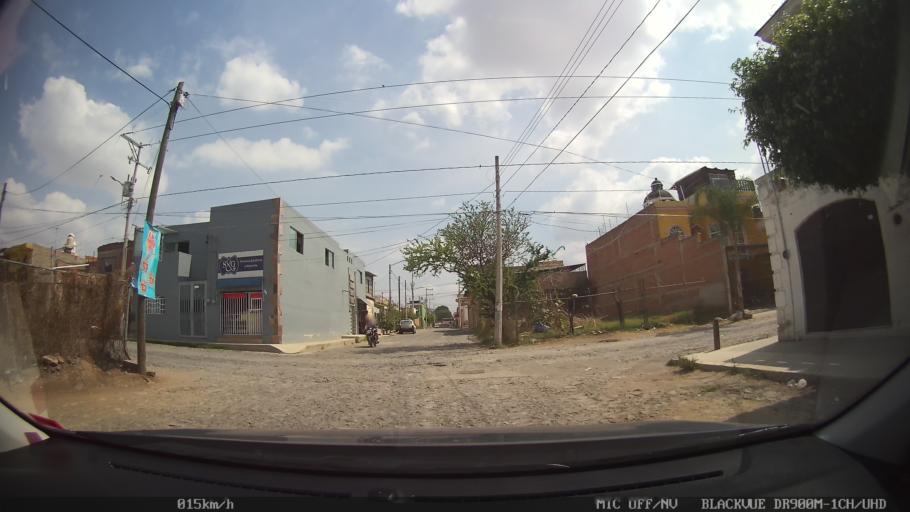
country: MX
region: Jalisco
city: Tonala
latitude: 20.6321
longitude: -103.2304
